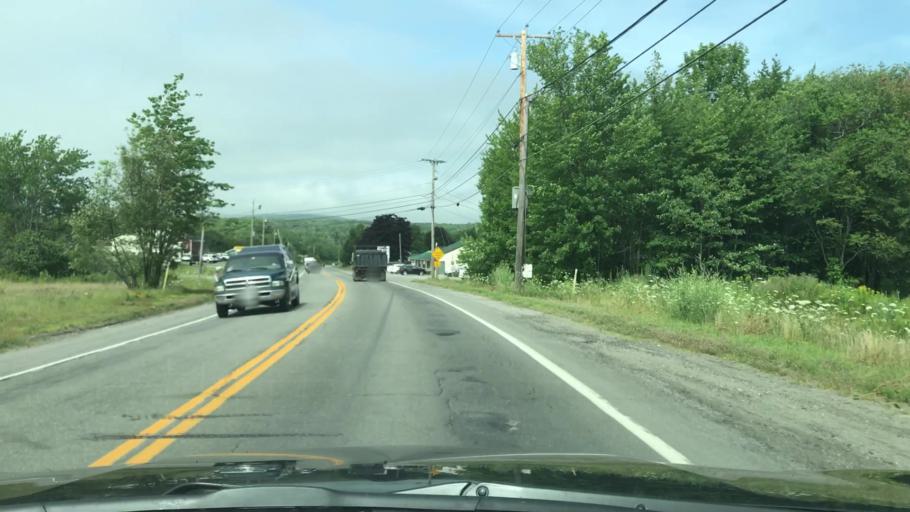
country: US
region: Maine
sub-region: Waldo County
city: Stockton Springs
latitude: 44.4644
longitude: -68.9033
